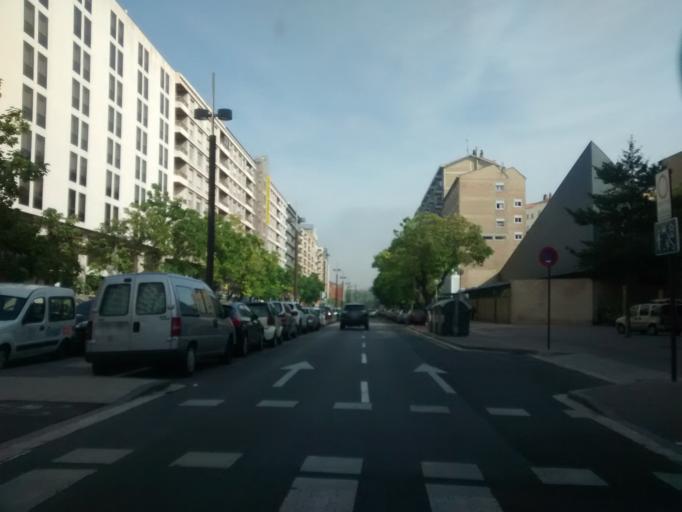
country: ES
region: Basque Country
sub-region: Provincia de Alava
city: Gasteiz / Vitoria
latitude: 42.8473
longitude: -2.6817
